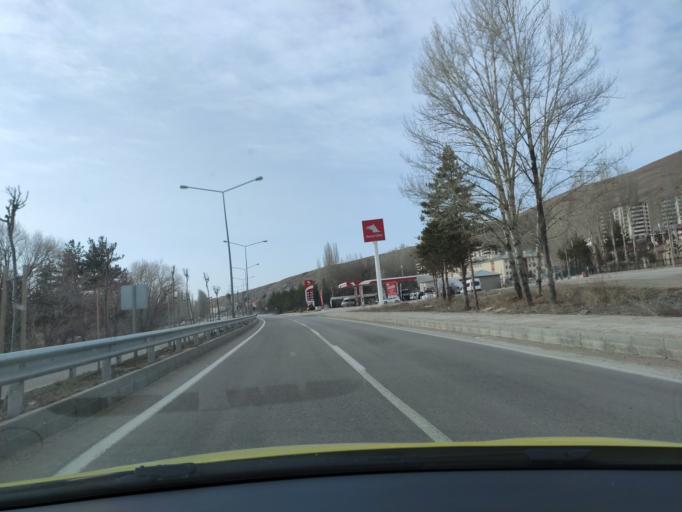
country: TR
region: Bayburt
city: Bayburt
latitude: 40.2386
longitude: 40.2509
